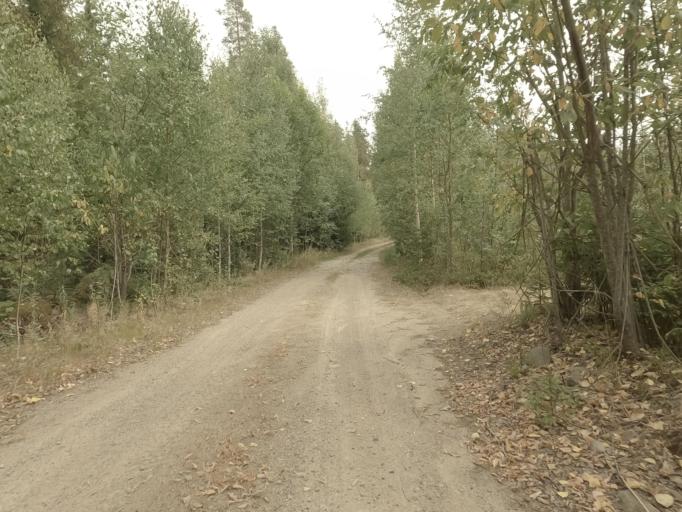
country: RU
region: Leningrad
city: Kamennogorsk
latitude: 61.0155
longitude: 29.2067
